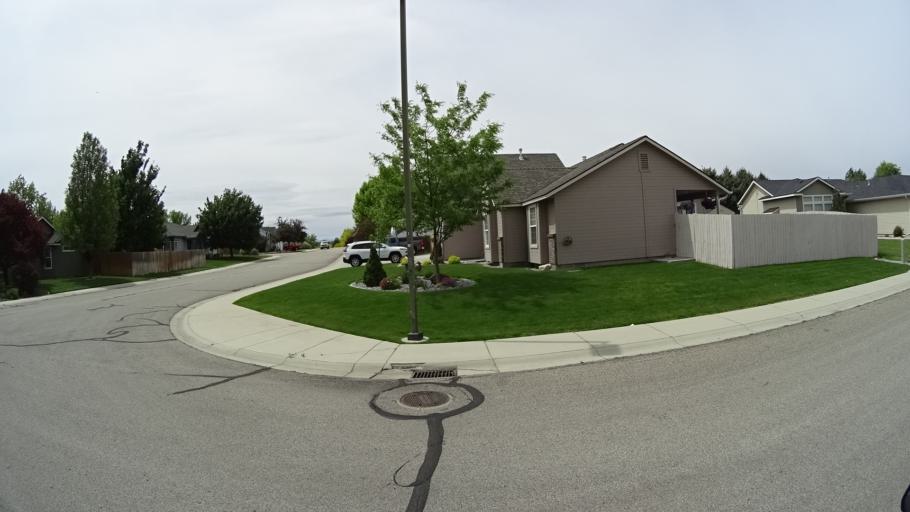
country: US
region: Idaho
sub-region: Ada County
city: Meridian
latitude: 43.5552
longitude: -116.3366
